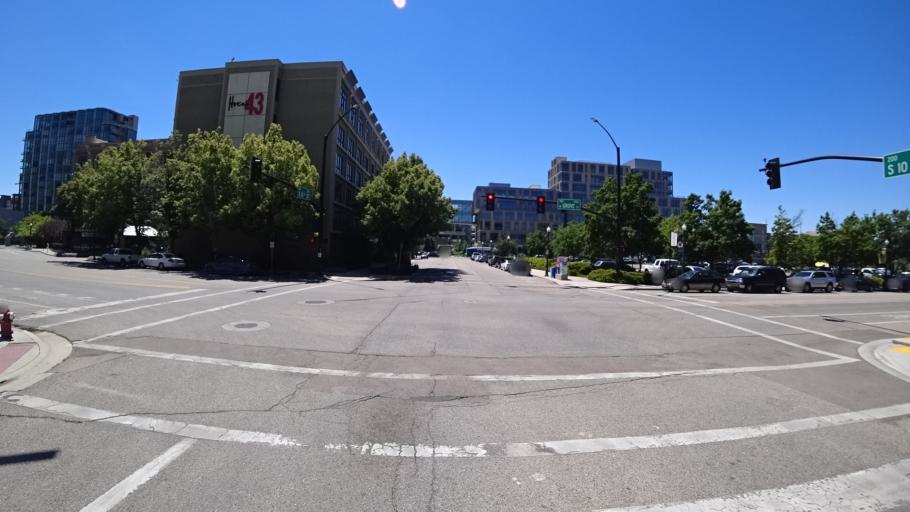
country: US
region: Idaho
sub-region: Ada County
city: Boise
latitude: 43.6162
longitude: -116.2065
